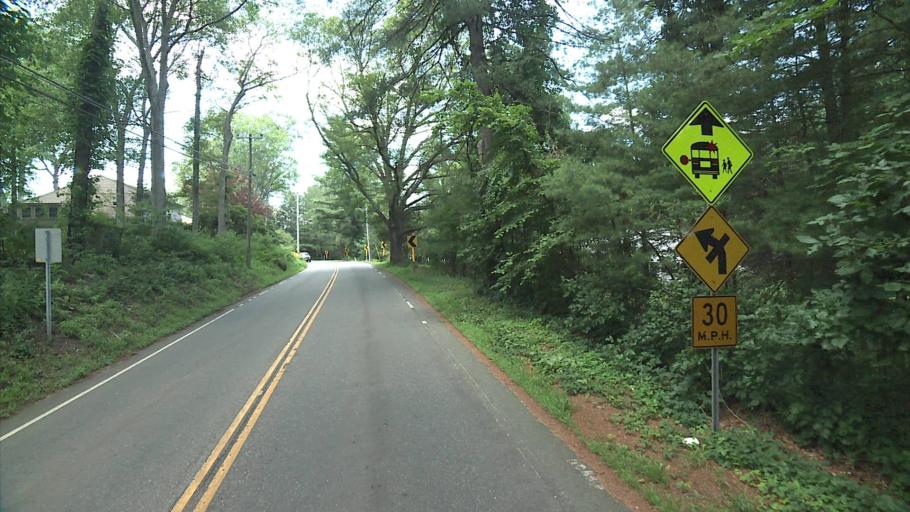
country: US
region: Connecticut
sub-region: Windham County
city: Windham
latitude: 41.7142
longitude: -72.1757
